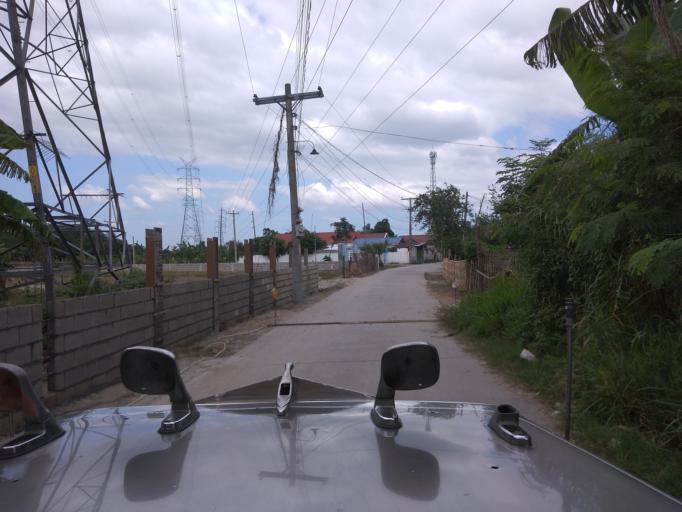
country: PH
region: Central Luzon
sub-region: Province of Pampanga
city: Malino
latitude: 15.1159
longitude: 120.6975
